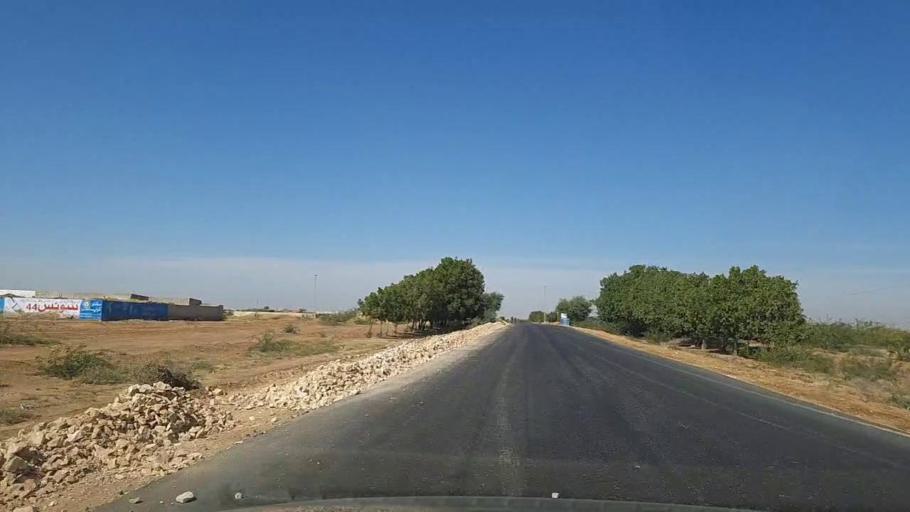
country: PK
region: Sindh
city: Kotri
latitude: 25.2502
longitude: 68.2277
